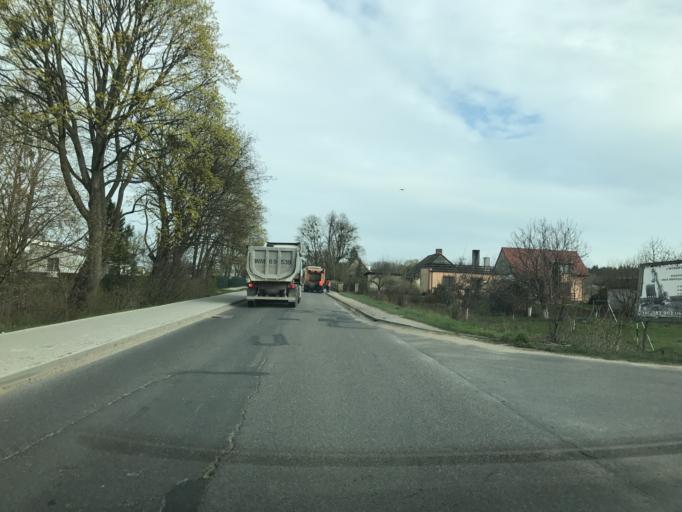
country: PL
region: Warmian-Masurian Voivodeship
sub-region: Powiat ostrodzki
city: Gierzwald
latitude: 53.5388
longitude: 20.0892
